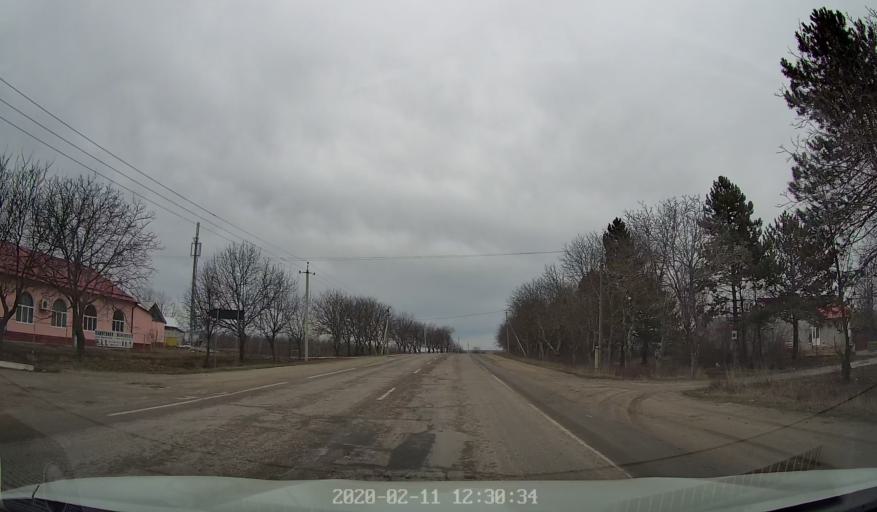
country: MD
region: Raionul Edinet
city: Edinet
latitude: 48.1653
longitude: 27.2820
